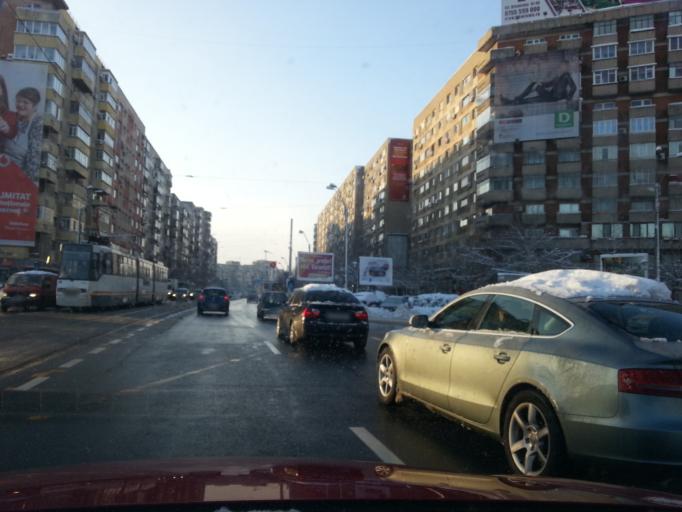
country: RO
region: Bucuresti
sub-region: Municipiul Bucuresti
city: Bucharest
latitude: 44.4240
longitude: 26.1373
